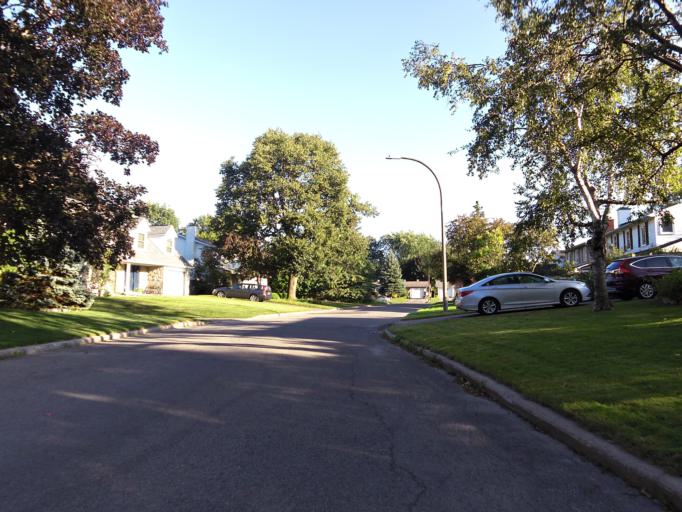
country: CA
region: Ontario
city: Ottawa
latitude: 45.3541
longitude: -75.7229
